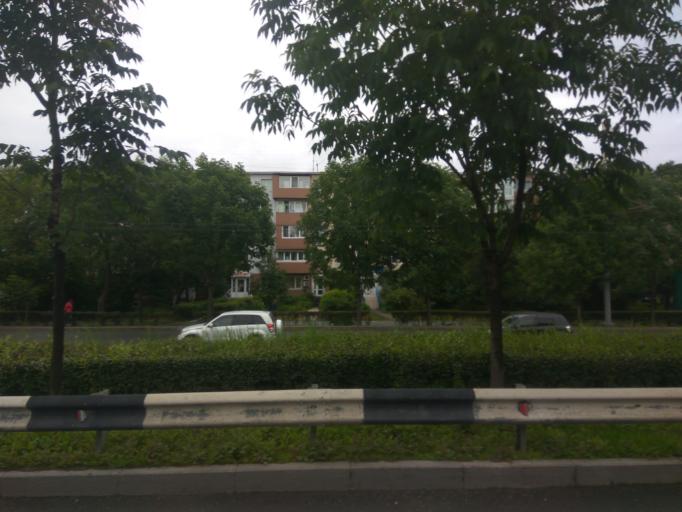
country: RU
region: Primorskiy
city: Vladivostok
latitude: 43.1627
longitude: 131.9129
